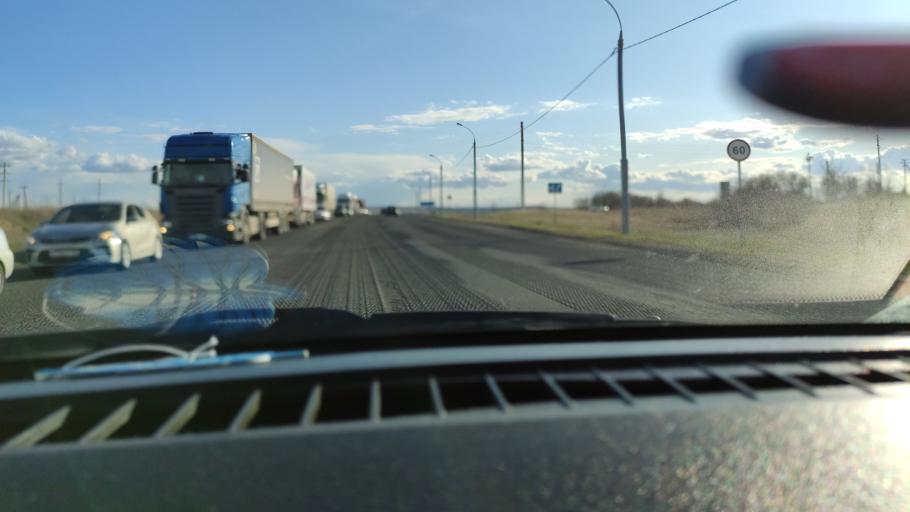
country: RU
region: Saratov
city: Yelshanka
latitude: 51.8142
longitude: 46.2075
